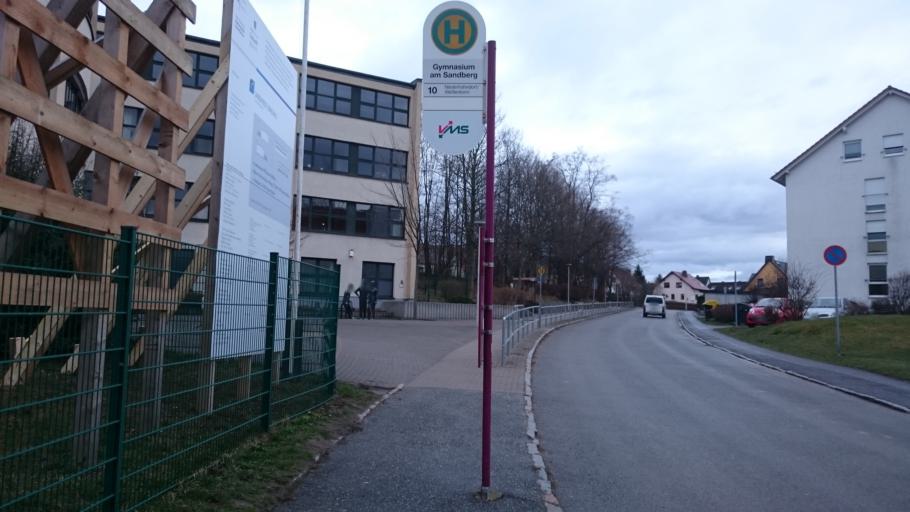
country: DE
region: Saxony
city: Wilkau-Hasslau
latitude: 50.6816
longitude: 12.5107
